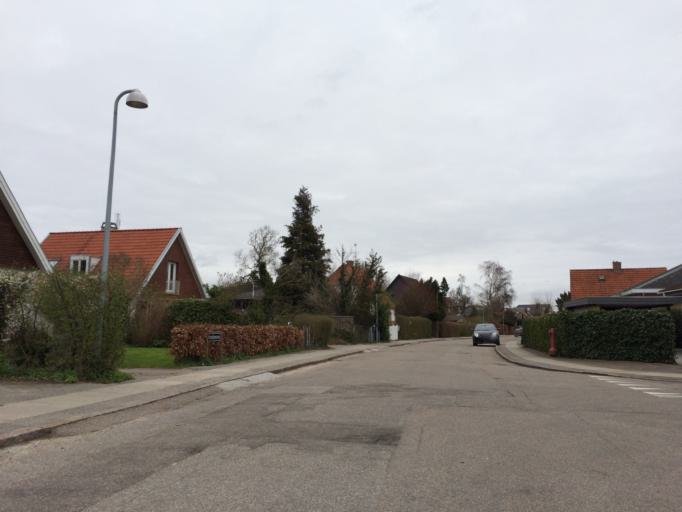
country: DK
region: Capital Region
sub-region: Hoje-Taastrup Kommune
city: Taastrup
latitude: 55.6504
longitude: 12.2954
